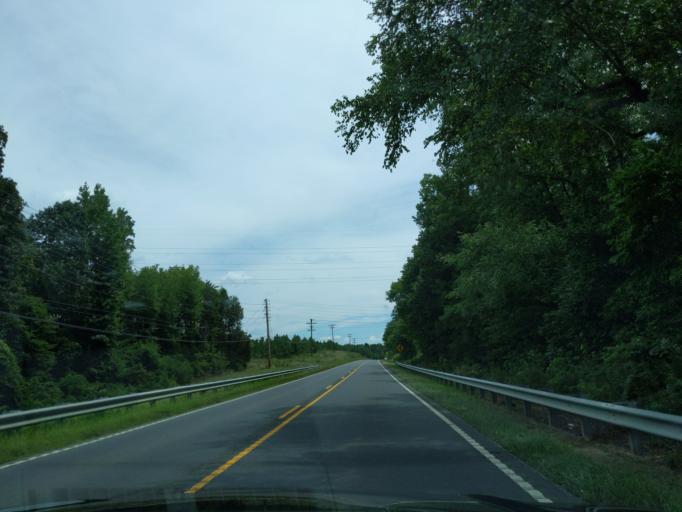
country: US
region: North Carolina
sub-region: Rowan County
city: Rockwell
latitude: 35.4674
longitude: -80.2913
